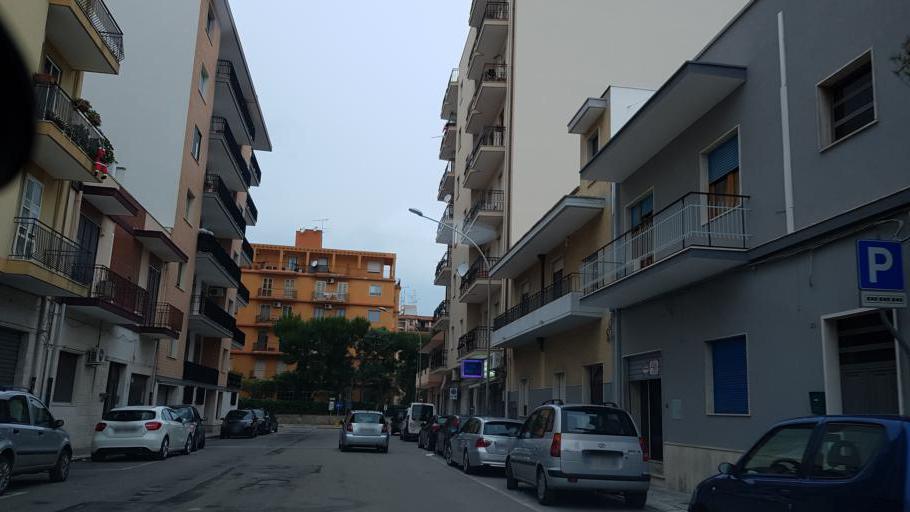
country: IT
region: Apulia
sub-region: Provincia di Brindisi
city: Brindisi
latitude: 40.6314
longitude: 17.9242
